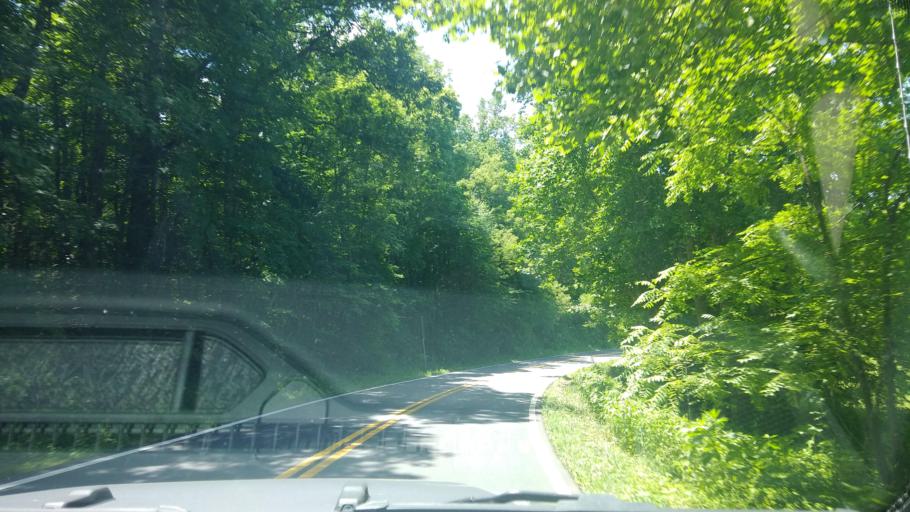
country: US
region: Tennessee
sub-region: Cocke County
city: Newport
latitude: 35.7852
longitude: -83.1954
